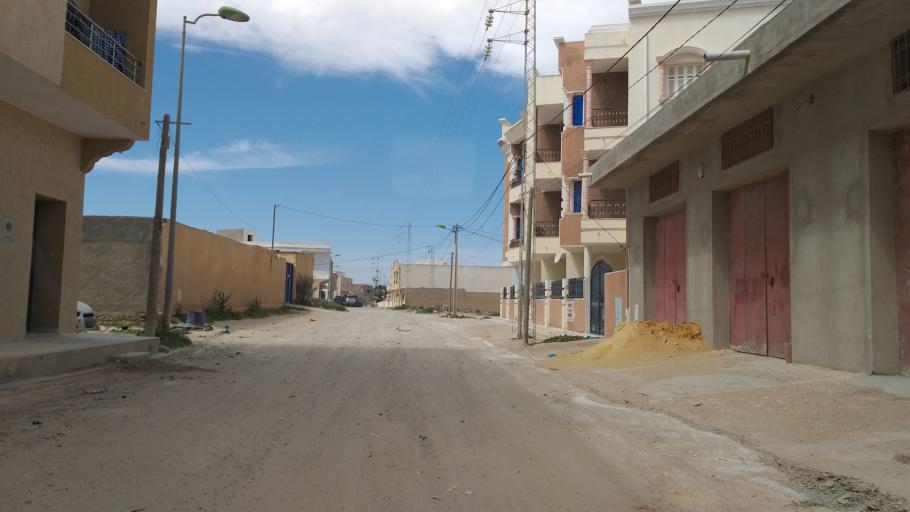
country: TN
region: Al Mahdiyah
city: El Jem
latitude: 35.3027
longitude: 10.6970
